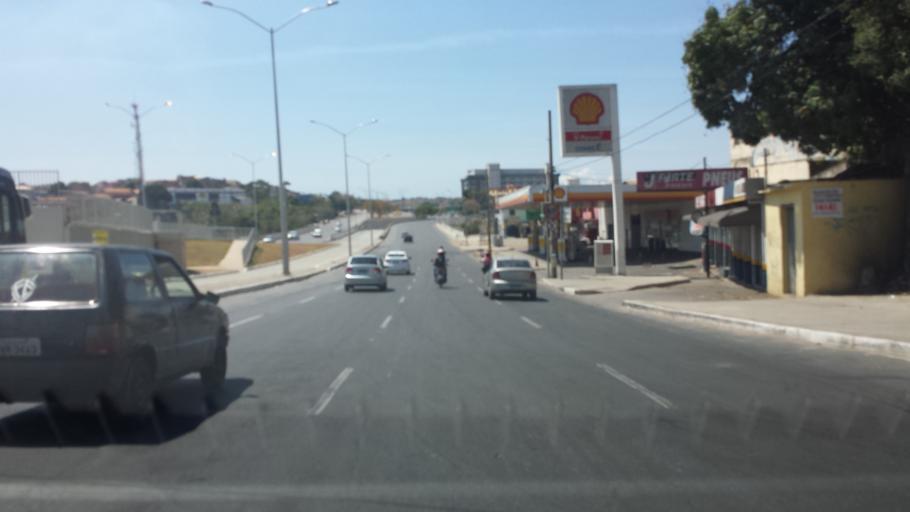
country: BR
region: Minas Gerais
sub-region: Belo Horizonte
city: Belo Horizonte
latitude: -19.8216
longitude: -43.9527
